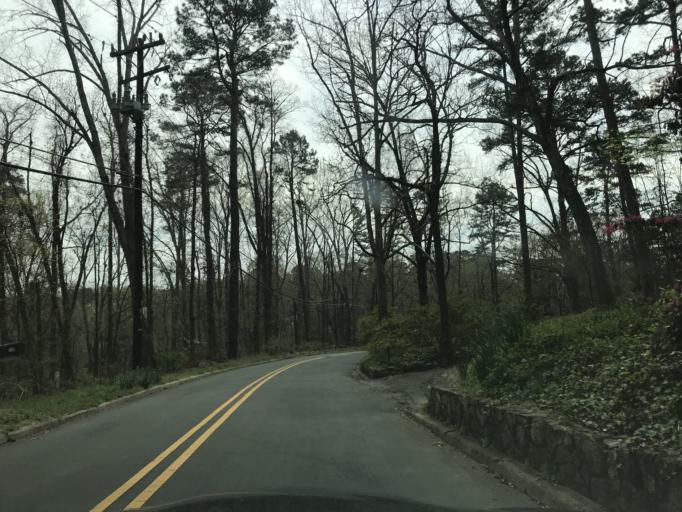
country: US
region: North Carolina
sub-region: Orange County
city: Chapel Hill
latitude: 35.9079
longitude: -79.0394
